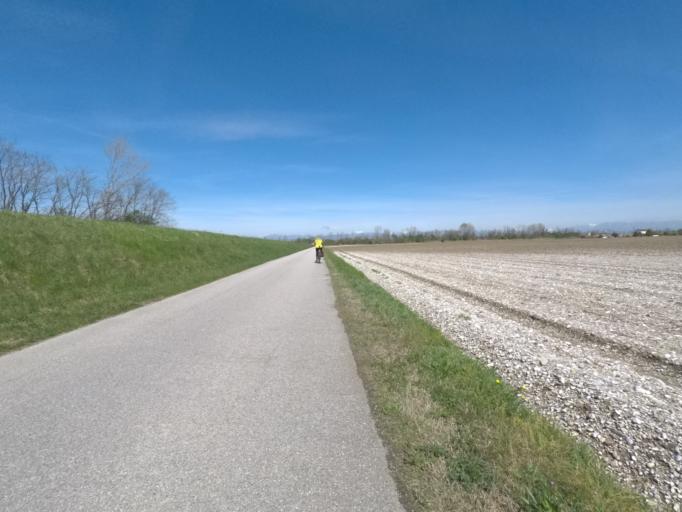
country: IT
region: Friuli Venezia Giulia
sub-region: Provincia di Udine
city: Camino al Tagliamento
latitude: 45.9556
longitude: 12.9136
